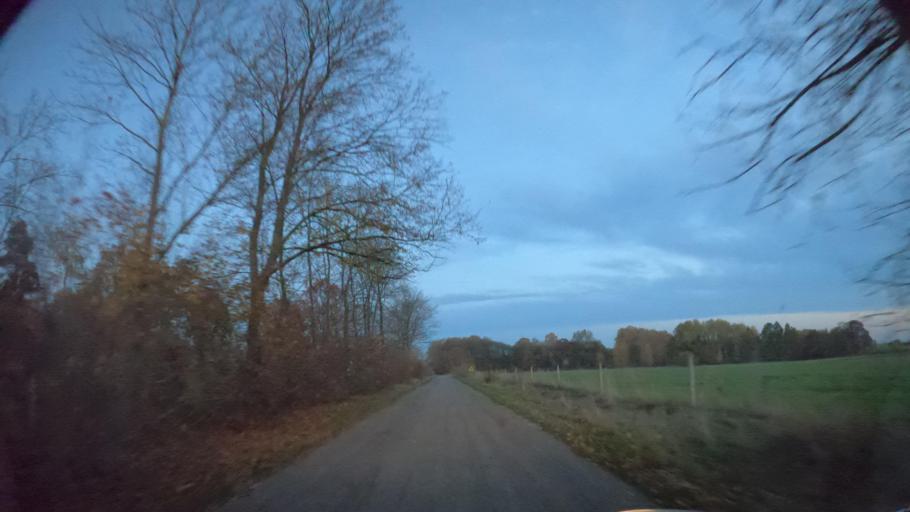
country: PL
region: Greater Poland Voivodeship
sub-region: Powiat zlotowski
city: Sypniewo
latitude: 53.4254
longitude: 16.6376
